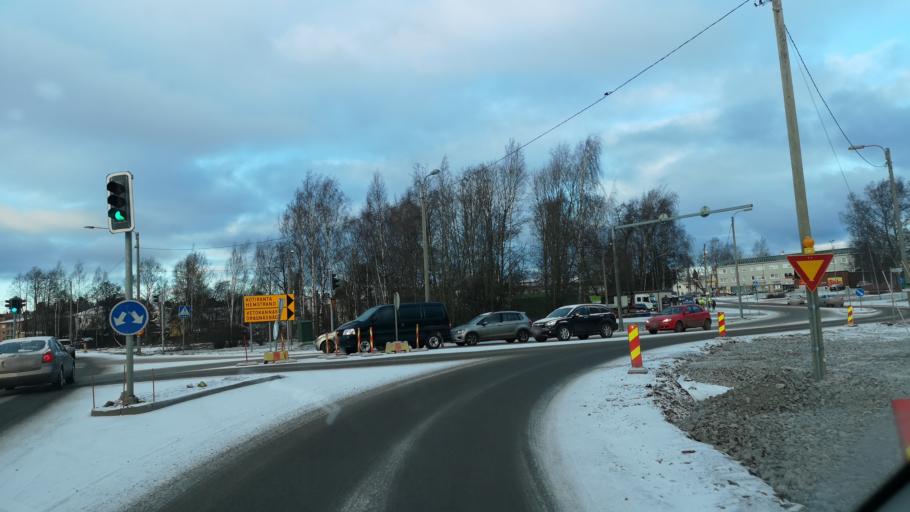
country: FI
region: Ostrobothnia
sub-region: Vaasa
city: Vaasa
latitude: 63.1134
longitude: 21.6180
